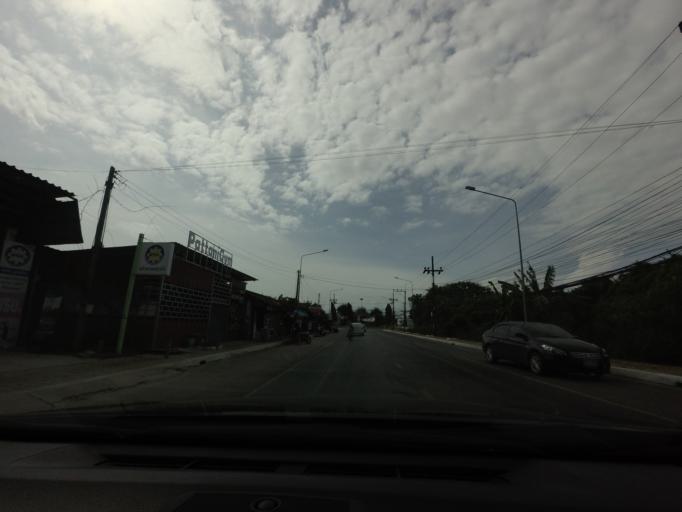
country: TH
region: Pattani
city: Pattani
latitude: 6.8820
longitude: 101.2456
